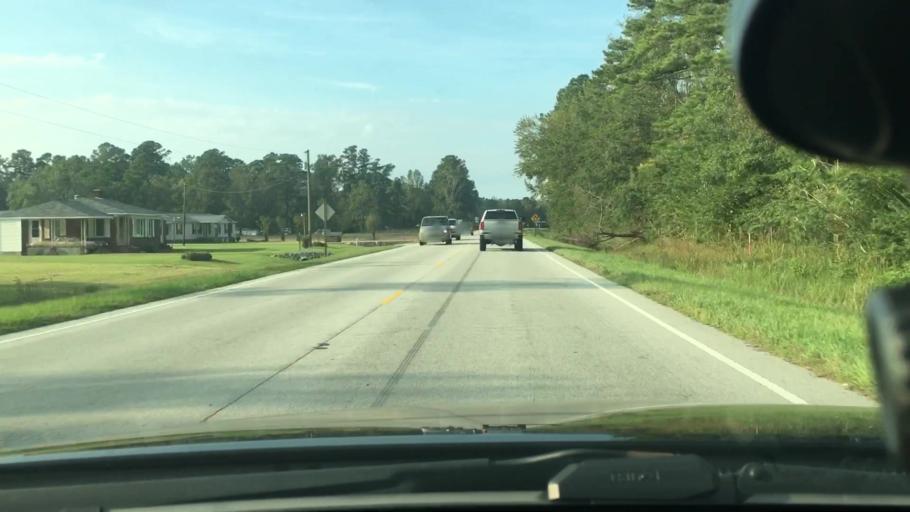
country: US
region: North Carolina
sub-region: Craven County
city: Vanceboro
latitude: 35.3286
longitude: -77.1489
